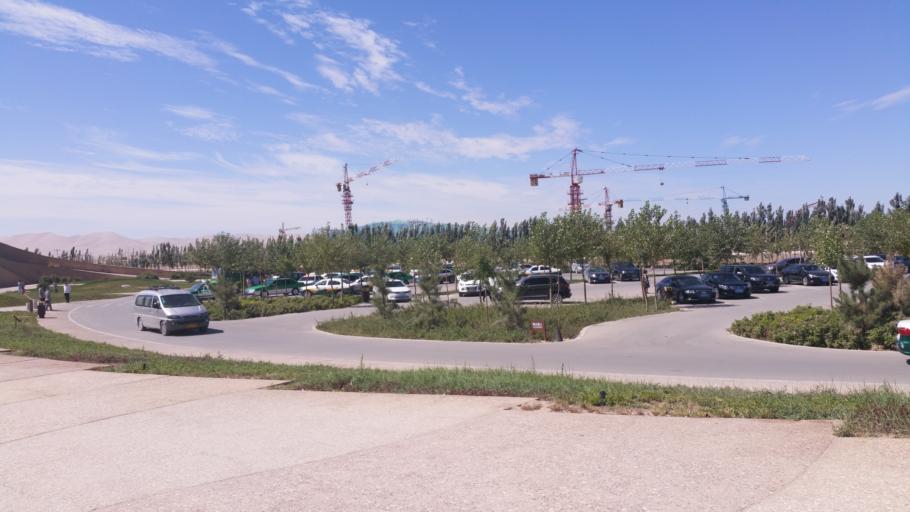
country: CN
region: Gansu Sheng
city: Guojiabao
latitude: 40.1615
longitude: 94.7653
